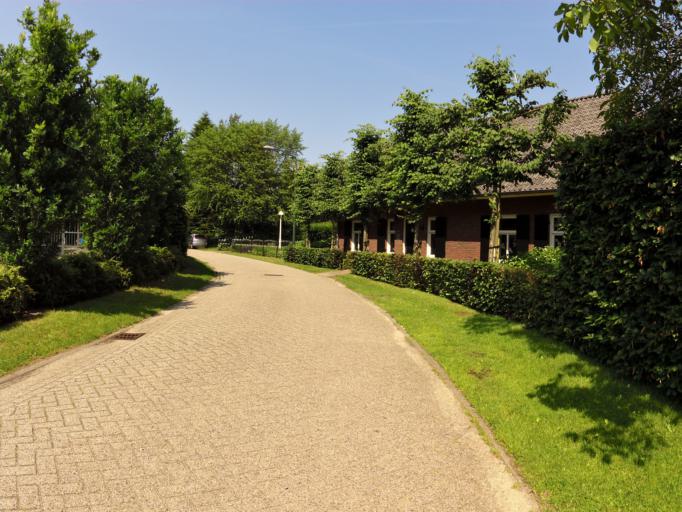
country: NL
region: North Brabant
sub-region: Gemeente Sint-Michielsgestel
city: Sint-Michielsgestel
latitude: 51.6366
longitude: 5.3582
